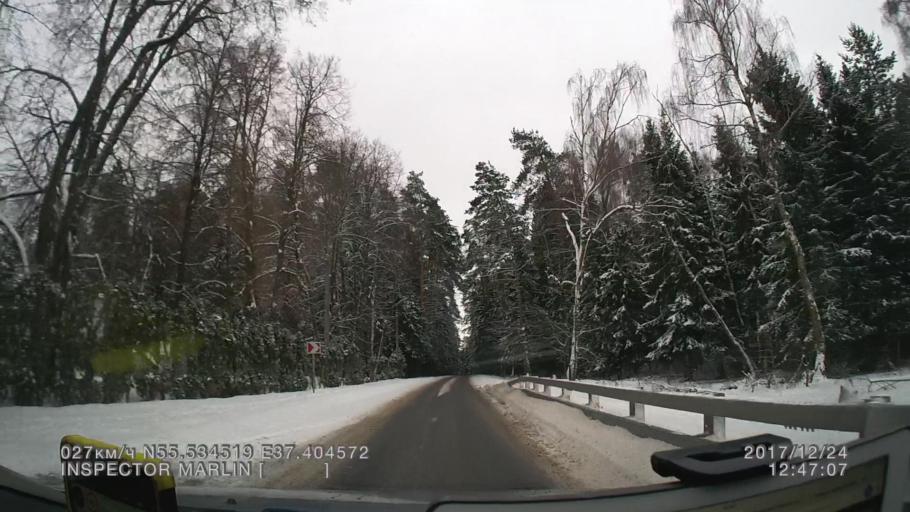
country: RU
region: Moskovskaya
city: Filimonki
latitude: 55.5345
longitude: 37.4046
